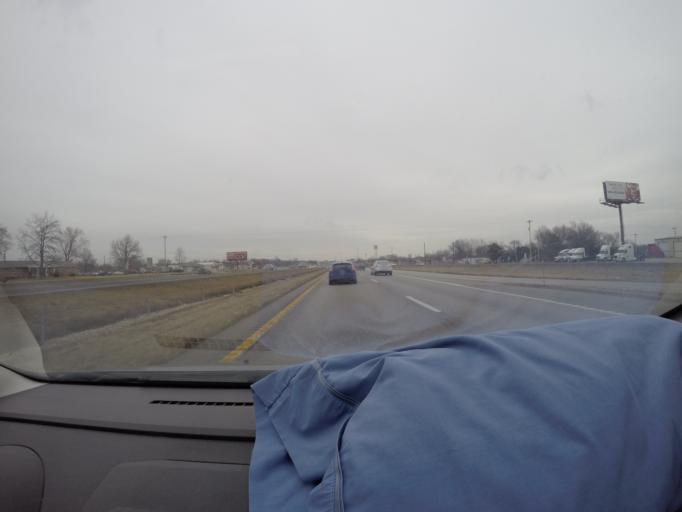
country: US
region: Missouri
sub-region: Warren County
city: Wright City
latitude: 38.8284
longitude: -91.0371
